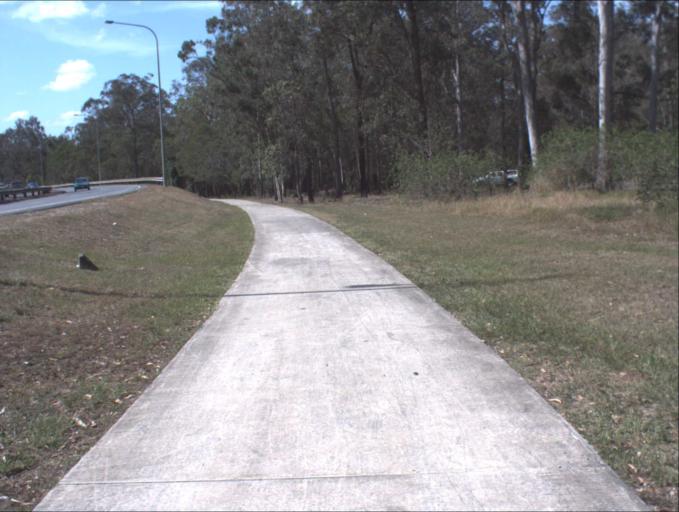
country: AU
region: Queensland
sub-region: Logan
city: Slacks Creek
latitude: -27.6545
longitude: 153.1458
